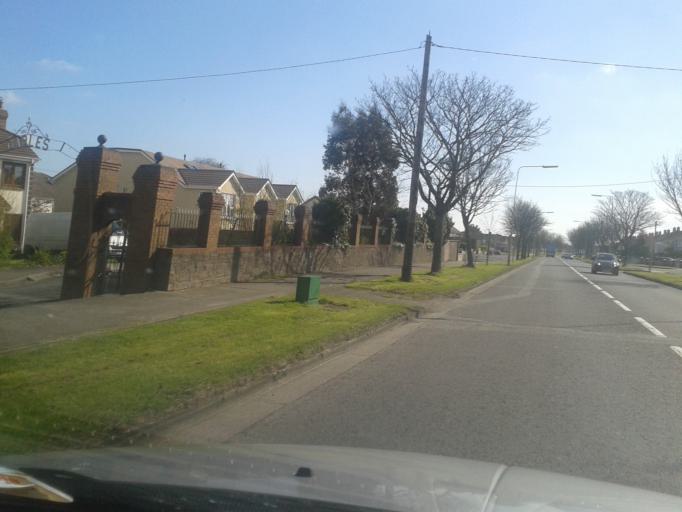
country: IE
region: Leinster
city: Raheny
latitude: 53.3912
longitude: -6.1755
